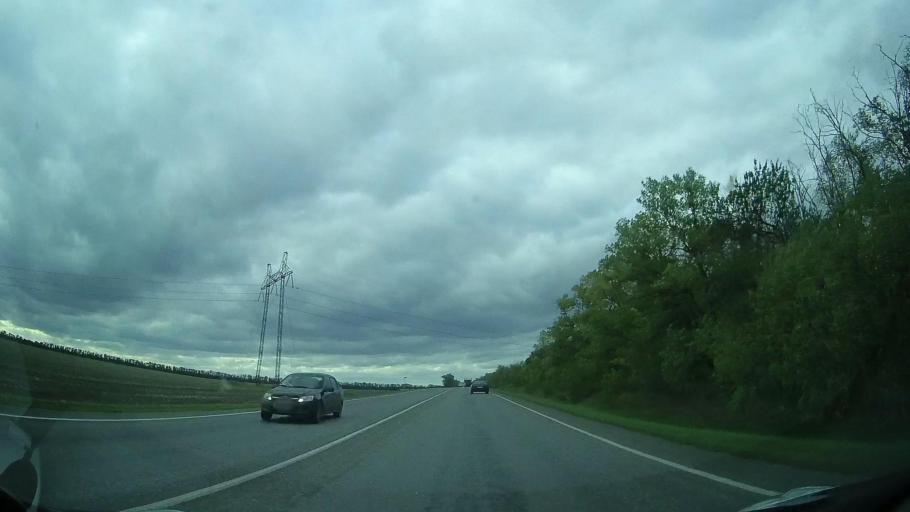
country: RU
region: Rostov
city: Zernograd
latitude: 46.8240
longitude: 40.2517
